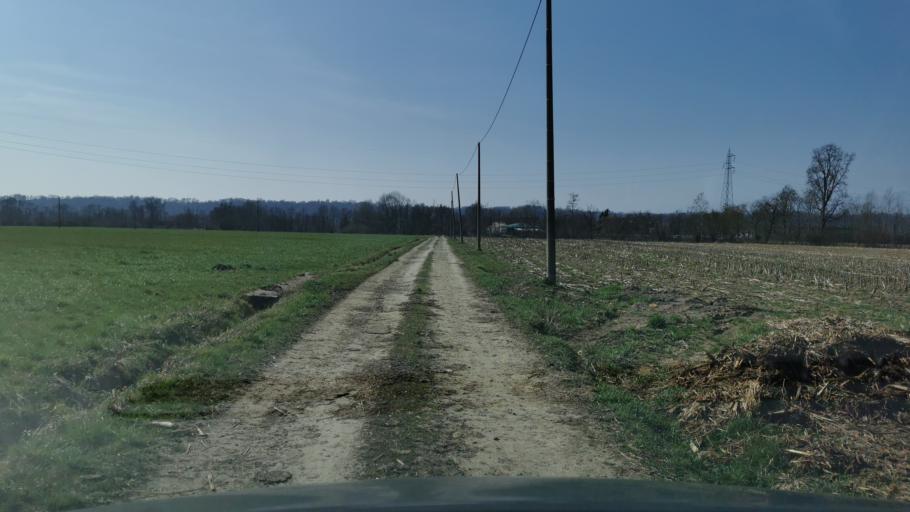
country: IT
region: Piedmont
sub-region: Provincia di Torino
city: Rivarossa
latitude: 45.2730
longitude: 7.7119
